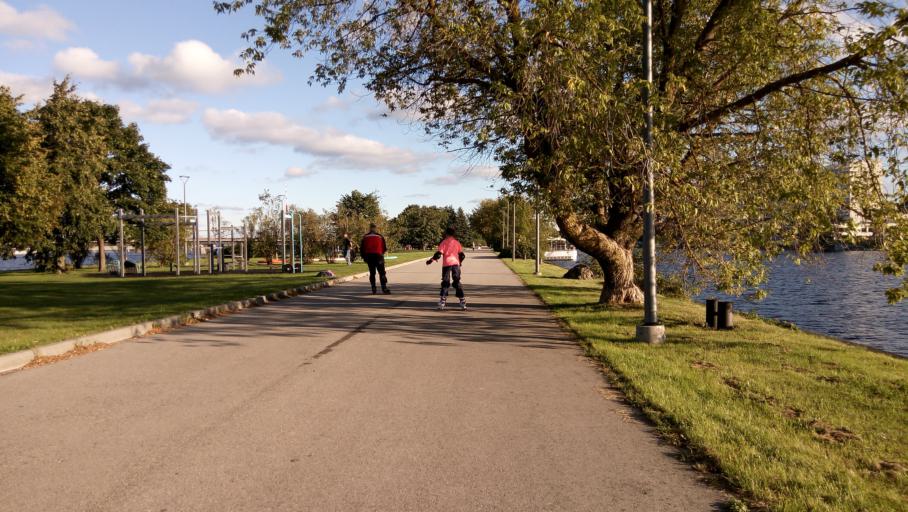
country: LV
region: Riga
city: Riga
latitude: 56.9474
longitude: 24.0933
